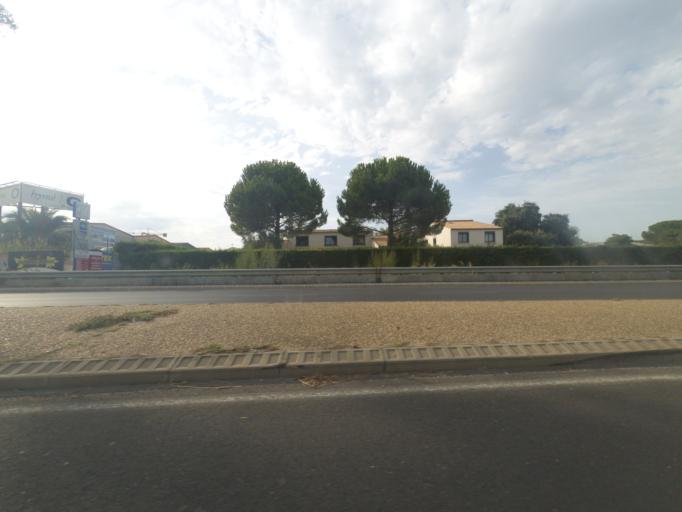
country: FR
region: Languedoc-Roussillon
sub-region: Departement de l'Herault
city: Castries
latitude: 43.6696
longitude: 3.9760
